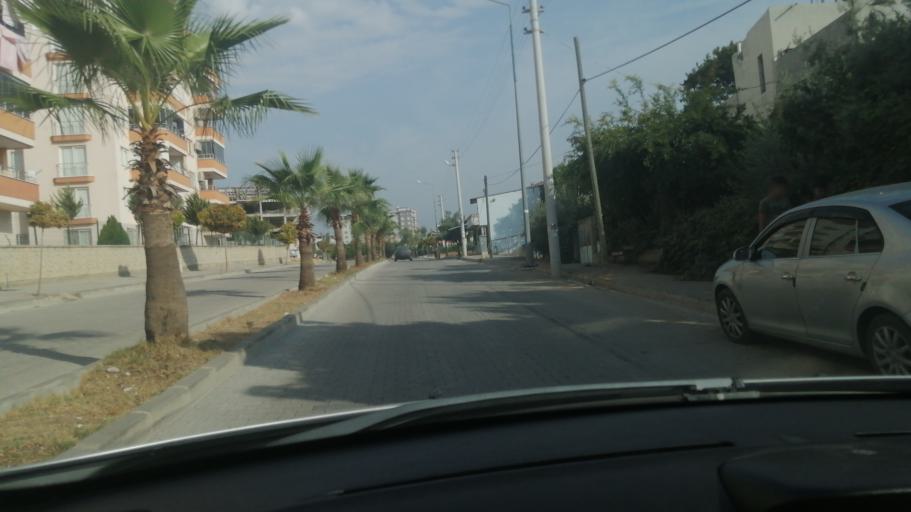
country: TR
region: Adana
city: Kadirli
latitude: 37.3723
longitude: 36.0794
